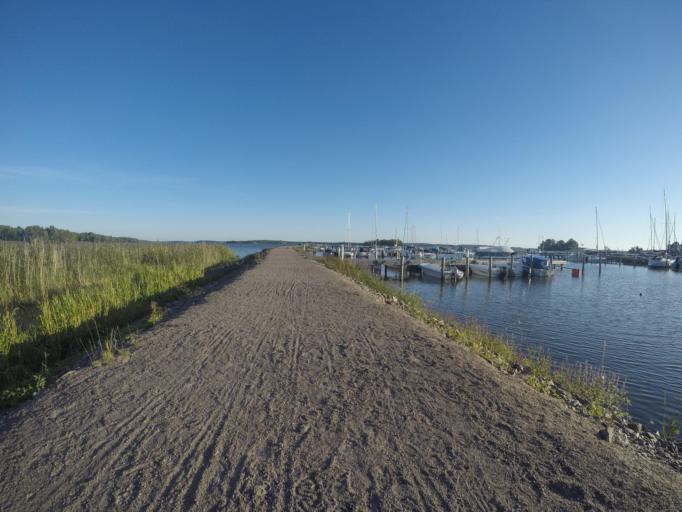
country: SE
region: Vaestmanland
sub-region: Vasteras
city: Vasteras
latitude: 59.5483
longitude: 16.6584
